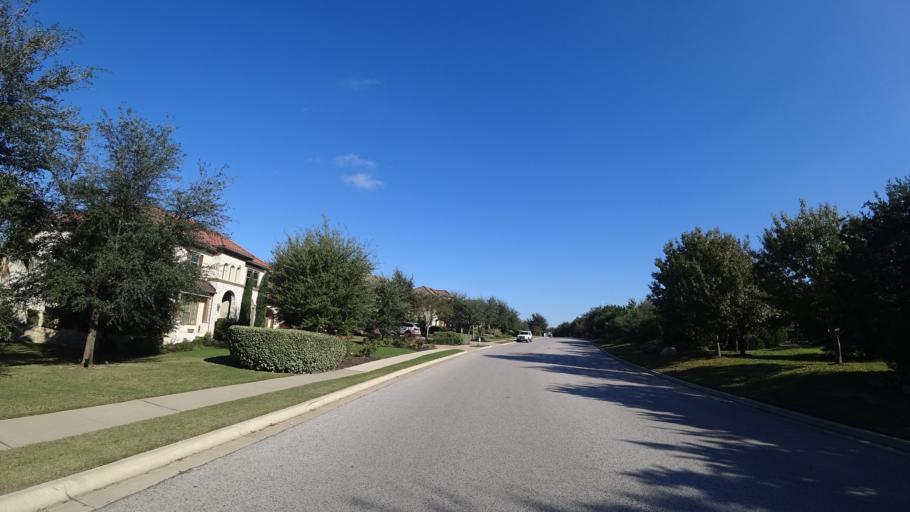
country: US
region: Texas
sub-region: Travis County
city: Bee Cave
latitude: 30.3529
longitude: -97.8938
